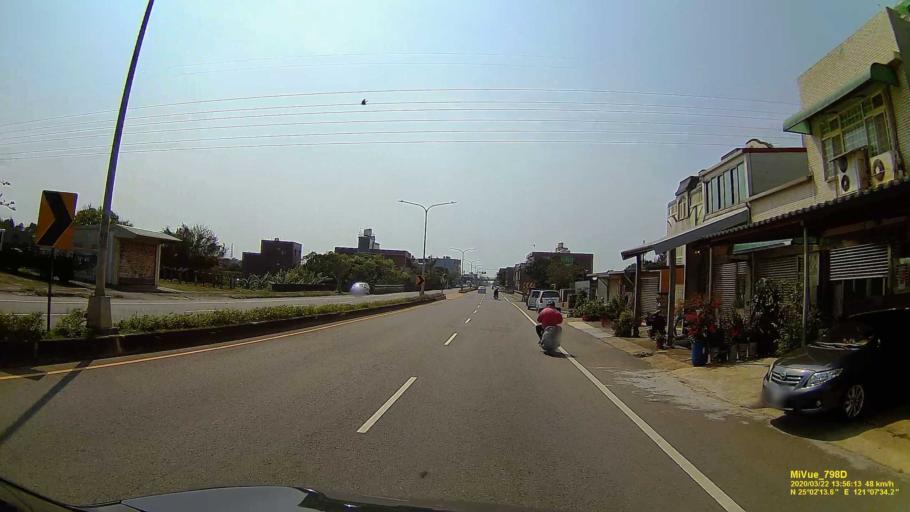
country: TW
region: Taiwan
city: Taoyuan City
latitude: 25.0371
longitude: 121.1259
